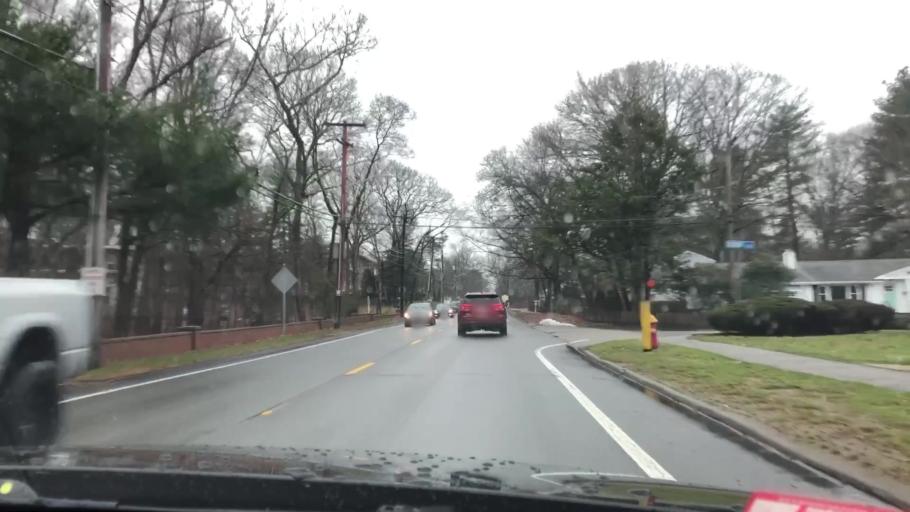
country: US
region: Massachusetts
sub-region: Norfolk County
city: Norwood
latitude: 42.1735
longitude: -71.2249
